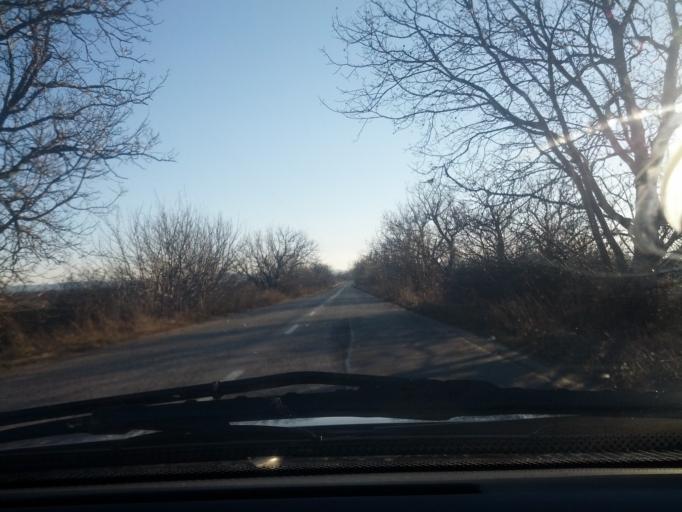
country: BG
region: Vratsa
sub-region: Obshtina Borovan
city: Borovan
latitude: 43.4835
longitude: 23.7946
